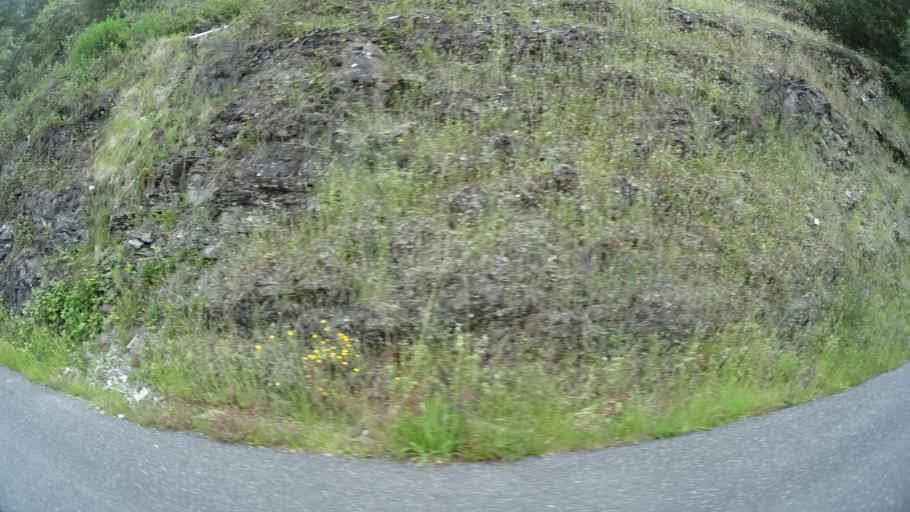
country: US
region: California
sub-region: Humboldt County
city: Willow Creek
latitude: 40.9464
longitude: -123.6110
